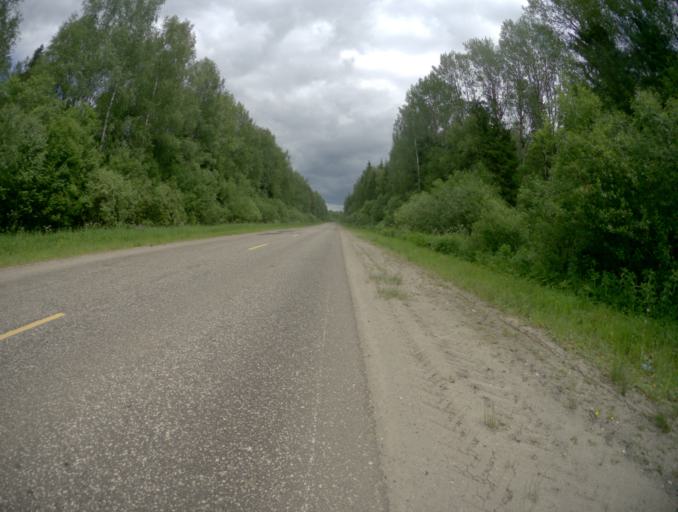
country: RU
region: Ivanovo
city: Arkhipovka
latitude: 56.6186
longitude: 41.2742
